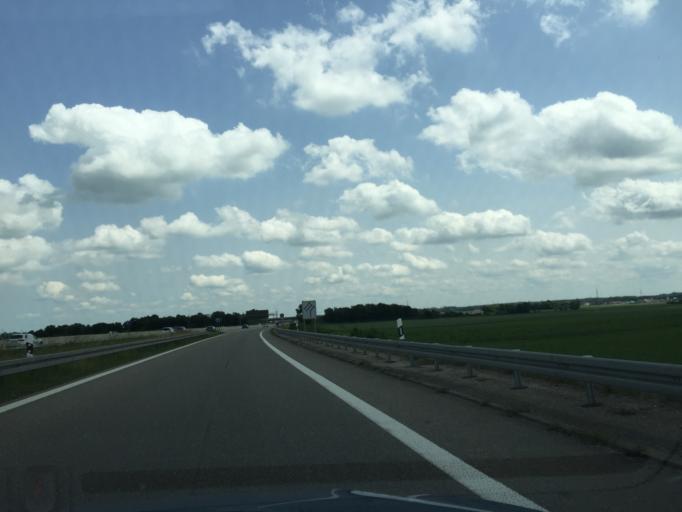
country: DE
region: Baden-Wuerttemberg
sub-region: Tuebingen Region
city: Langenau
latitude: 48.4642
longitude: 10.1215
